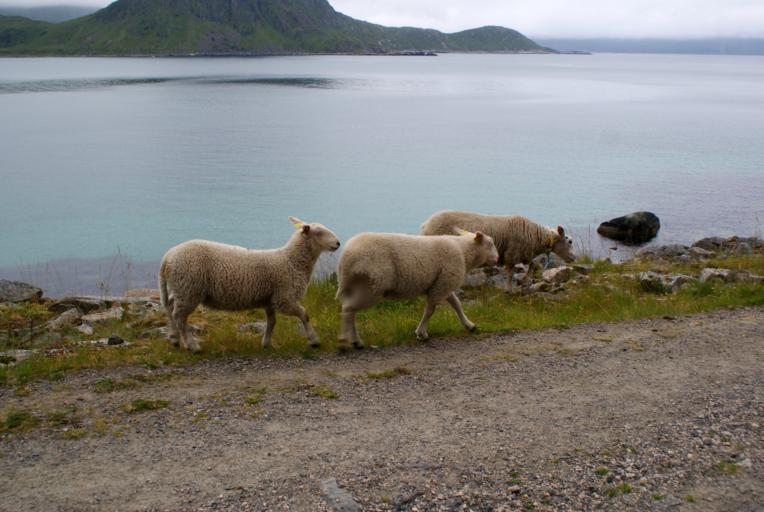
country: NO
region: Nordland
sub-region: Vestvagoy
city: Gravdal
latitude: 68.1990
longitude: 13.5051
